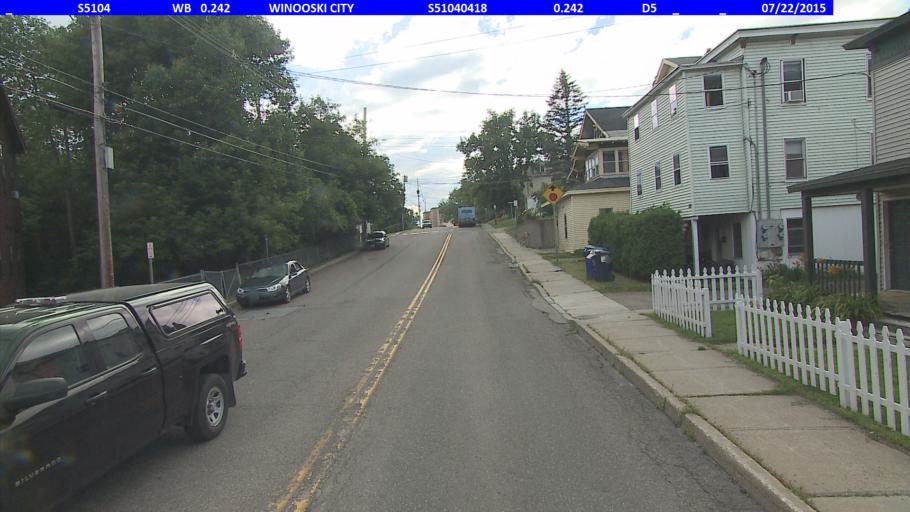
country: US
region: Vermont
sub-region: Chittenden County
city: Winooski
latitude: 44.4935
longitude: -73.1814
